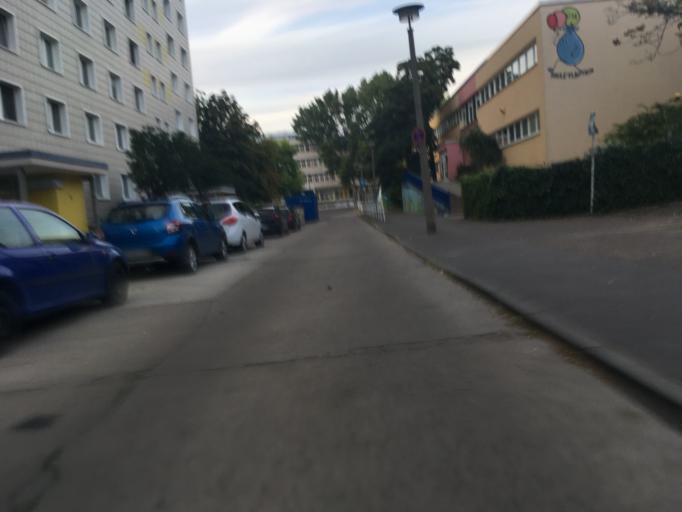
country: DE
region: Berlin
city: Fennpfuhl
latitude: 52.5305
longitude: 13.4809
